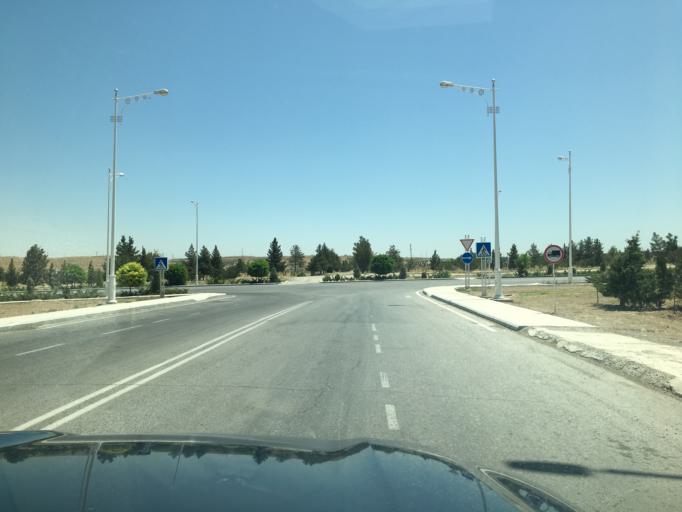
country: TM
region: Ahal
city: Ashgabat
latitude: 37.8508
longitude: 58.3752
